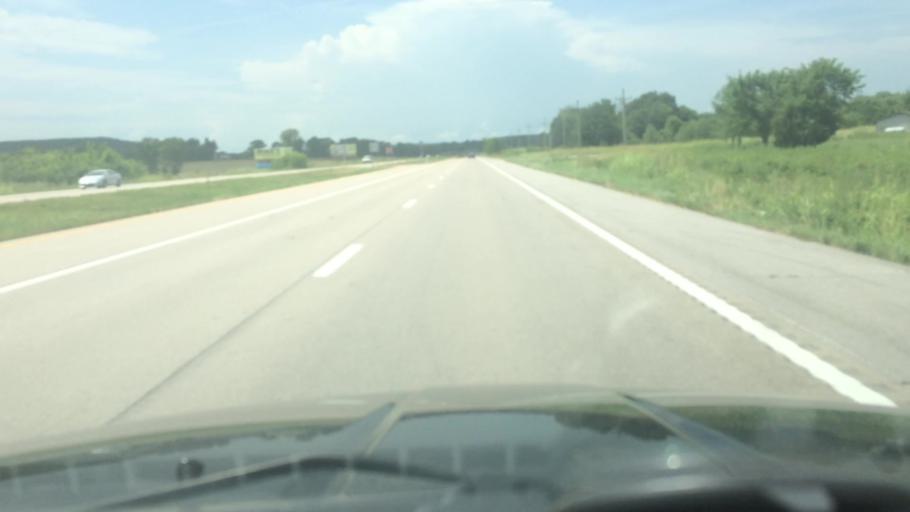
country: US
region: Missouri
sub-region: Polk County
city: Humansville
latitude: 37.8134
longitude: -93.6073
